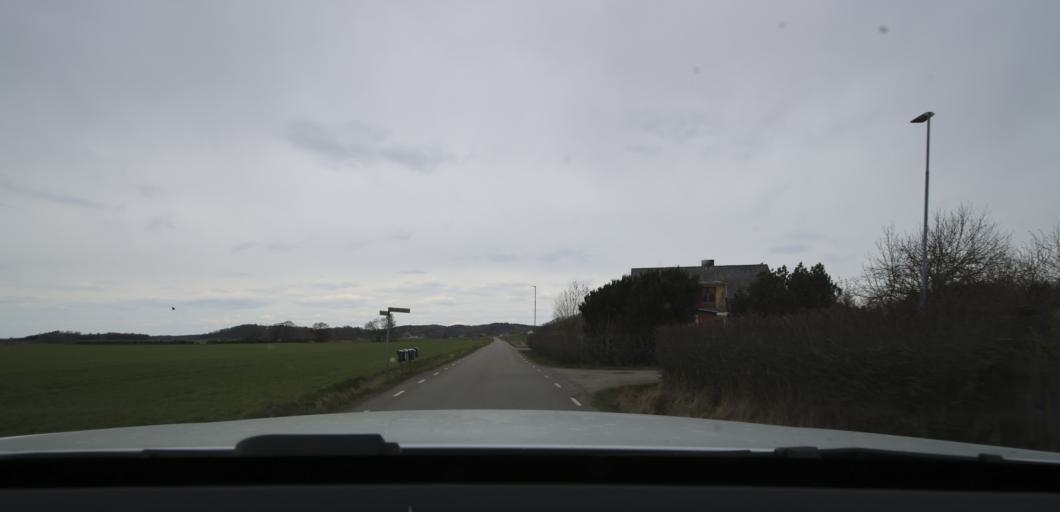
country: SE
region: Halland
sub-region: Varbergs Kommun
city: Tvaaker
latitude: 57.1345
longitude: 12.4510
